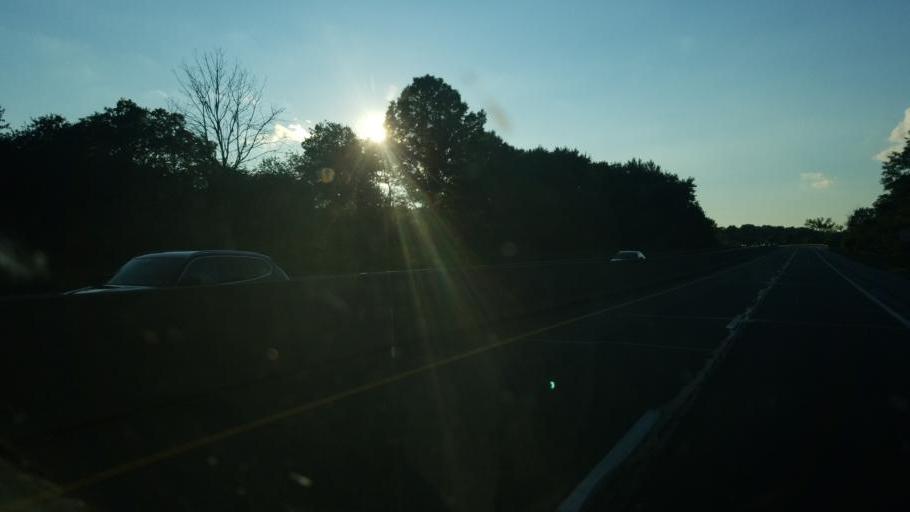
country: US
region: Ohio
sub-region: Mahoning County
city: New Middletown
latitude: 40.9121
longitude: -80.5204
